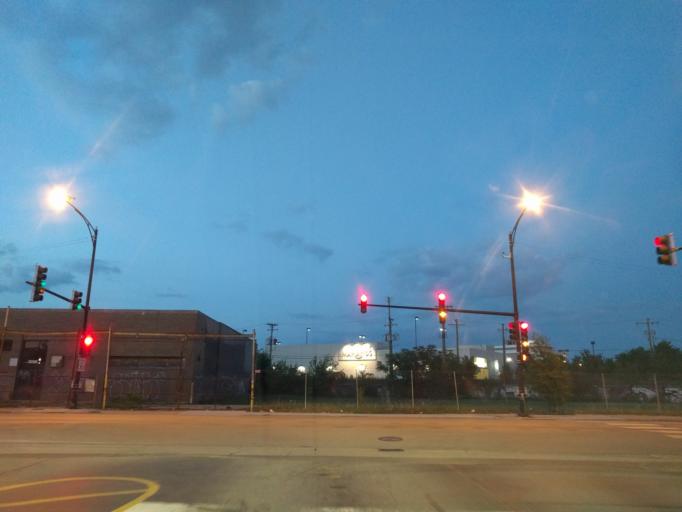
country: US
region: Illinois
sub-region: Cook County
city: Chicago
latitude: 41.9198
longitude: -87.6703
